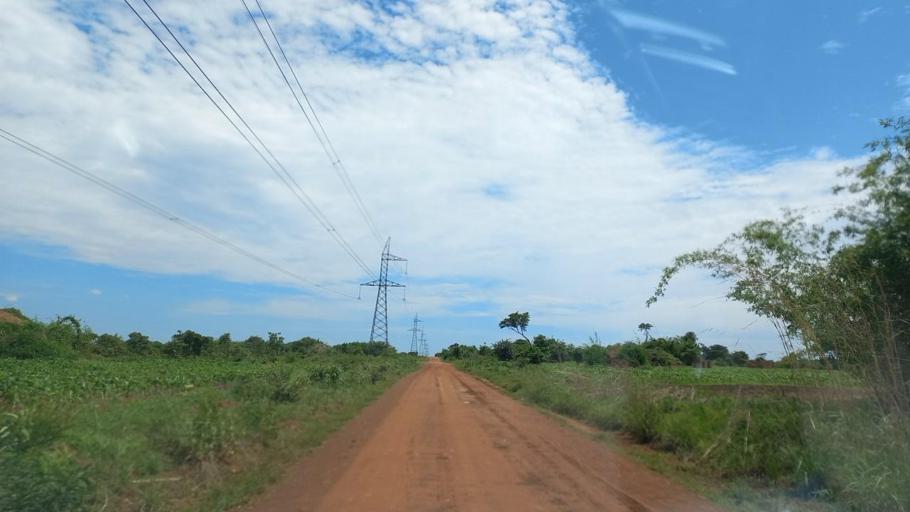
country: ZM
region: Copperbelt
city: Kitwe
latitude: -12.8489
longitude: 28.3344
